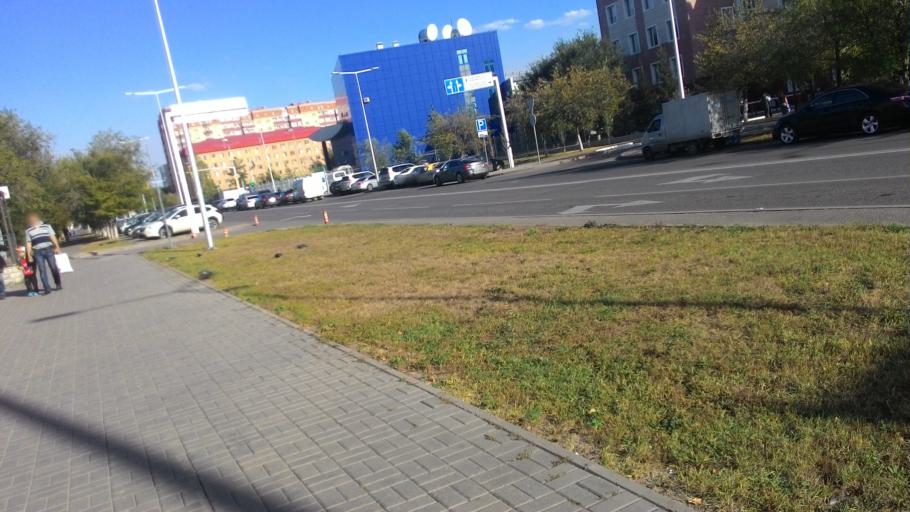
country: KZ
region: Astana Qalasy
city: Astana
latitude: 51.1819
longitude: 71.4098
